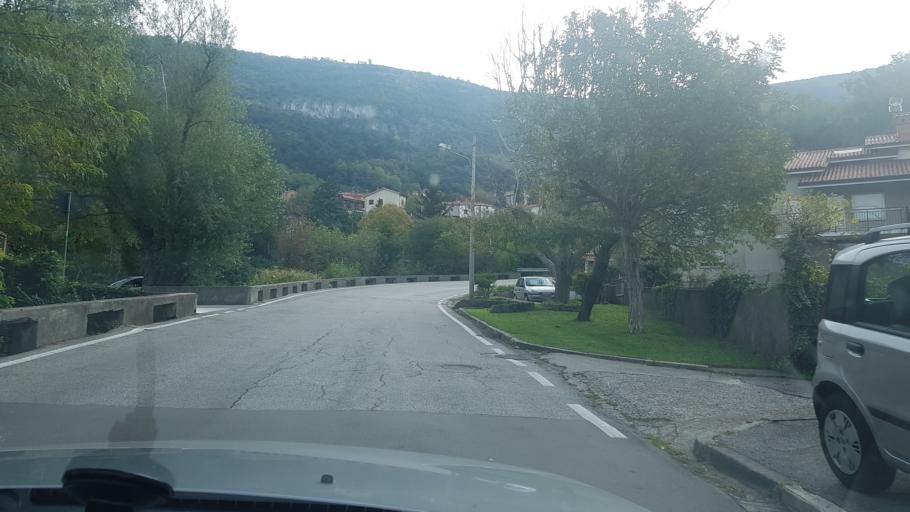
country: IT
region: Friuli Venezia Giulia
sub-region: Provincia di Trieste
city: Dolina
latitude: 45.6024
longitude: 13.8559
